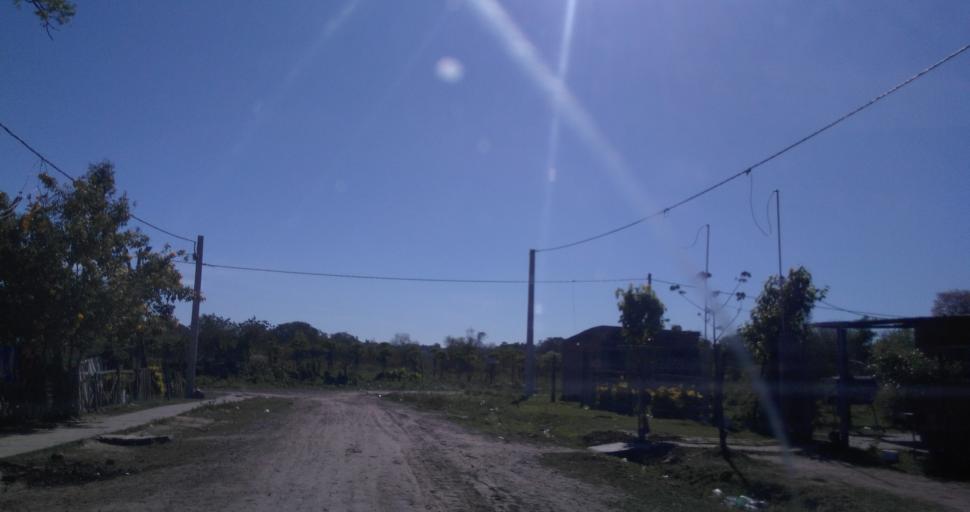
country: AR
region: Chaco
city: Fontana
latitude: -27.4166
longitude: -59.0192
